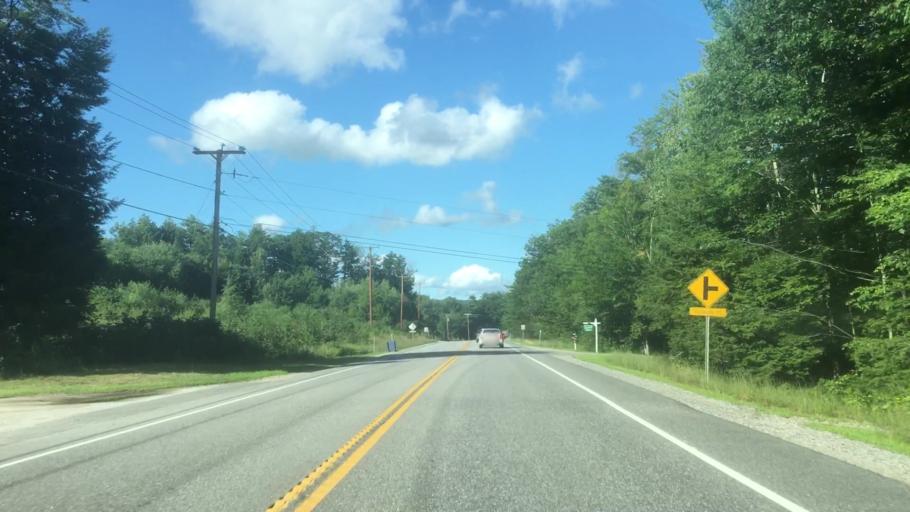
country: US
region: New Hampshire
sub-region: Hillsborough County
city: Hillsborough
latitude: 43.1109
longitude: -71.9552
